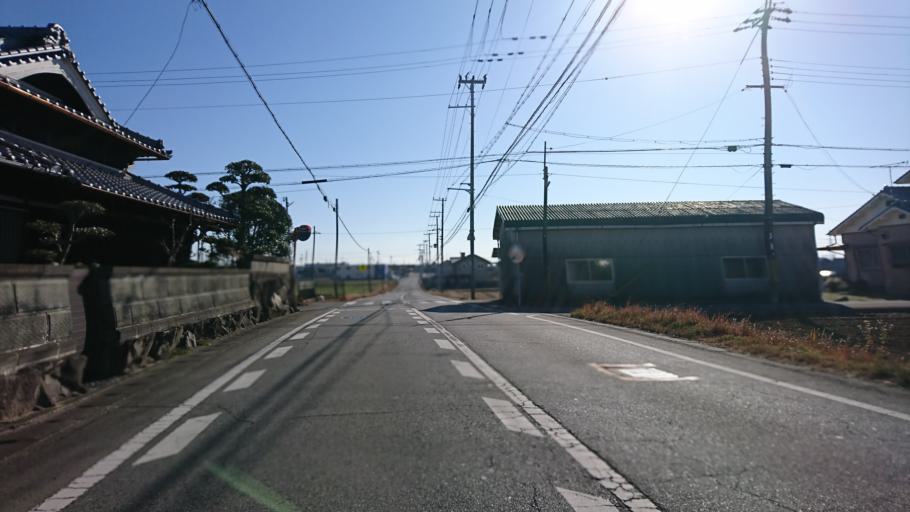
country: JP
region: Hyogo
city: Miki
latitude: 34.7500
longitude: 134.9284
